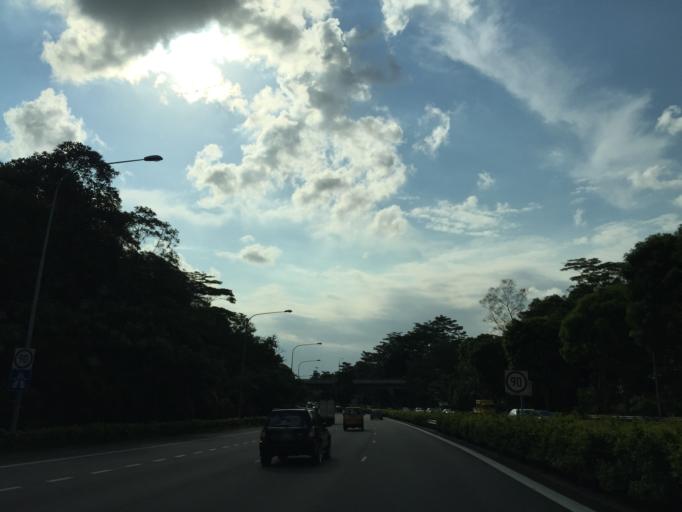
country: SG
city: Singapore
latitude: 1.3519
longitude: 103.7896
